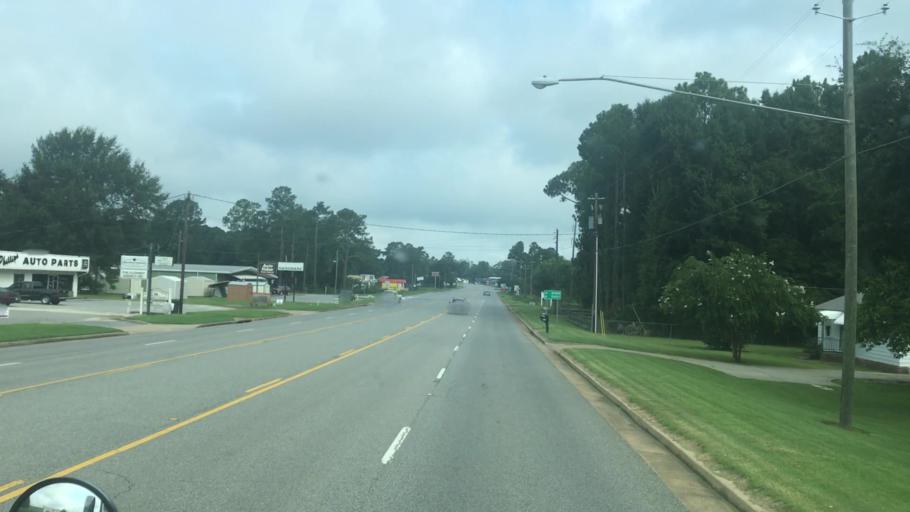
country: US
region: Georgia
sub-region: Miller County
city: Colquitt
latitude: 31.1644
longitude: -84.7218
